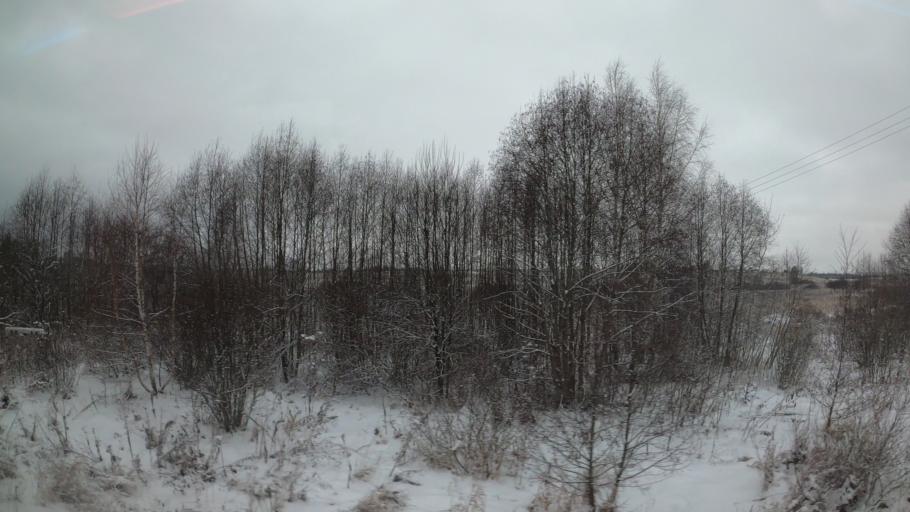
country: RU
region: Jaroslavl
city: Pereslavl'-Zalesskiy
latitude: 56.6934
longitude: 38.9158
